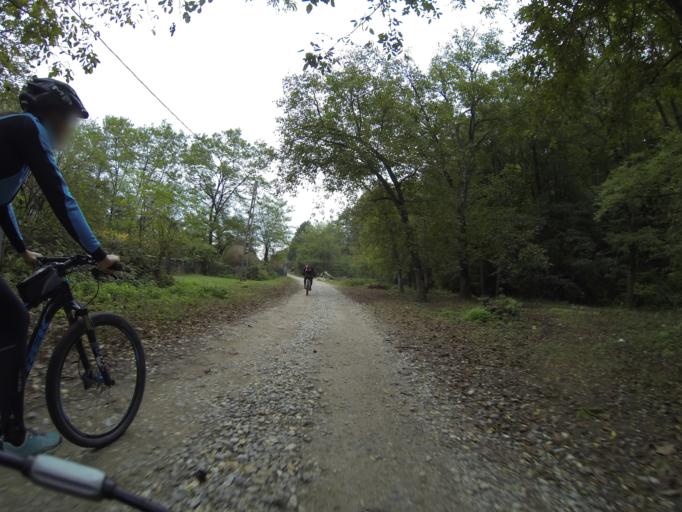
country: RO
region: Gorj
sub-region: Comuna Tismana
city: Pocruia
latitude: 45.0506
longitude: 22.9162
